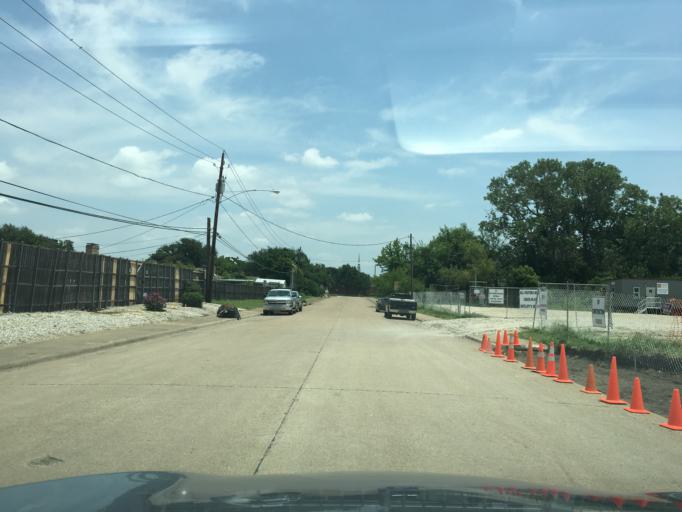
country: US
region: Texas
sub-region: Dallas County
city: Addison
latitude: 32.9211
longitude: -96.8098
